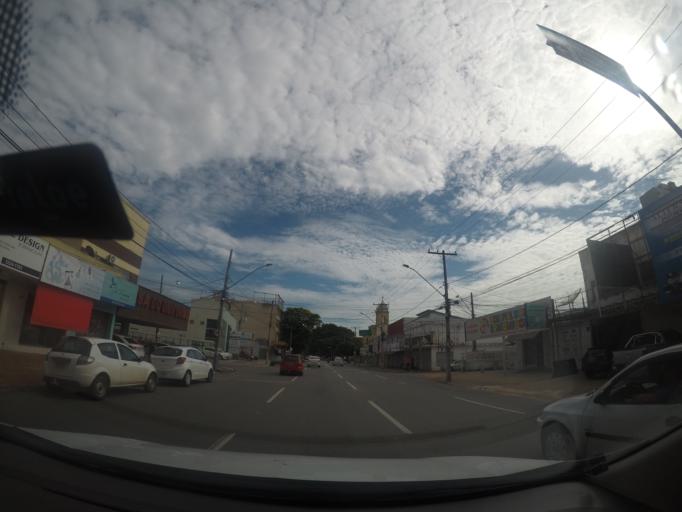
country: BR
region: Goias
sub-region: Goiania
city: Goiania
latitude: -16.6717
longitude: -49.2543
